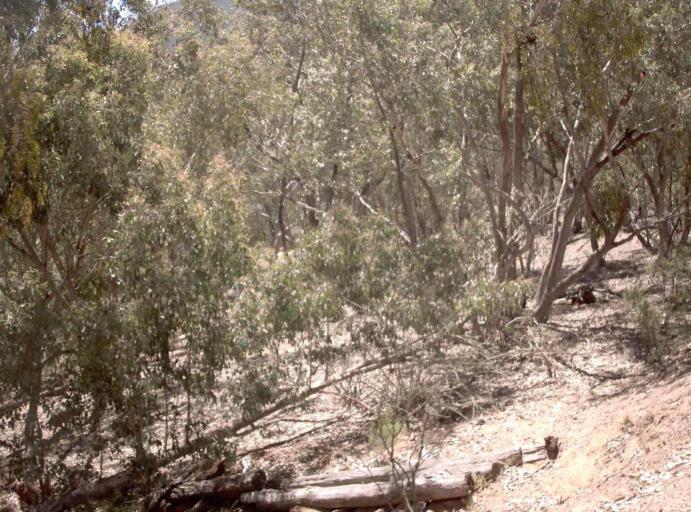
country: AU
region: New South Wales
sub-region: Snowy River
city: Jindabyne
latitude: -37.0897
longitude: 148.4426
